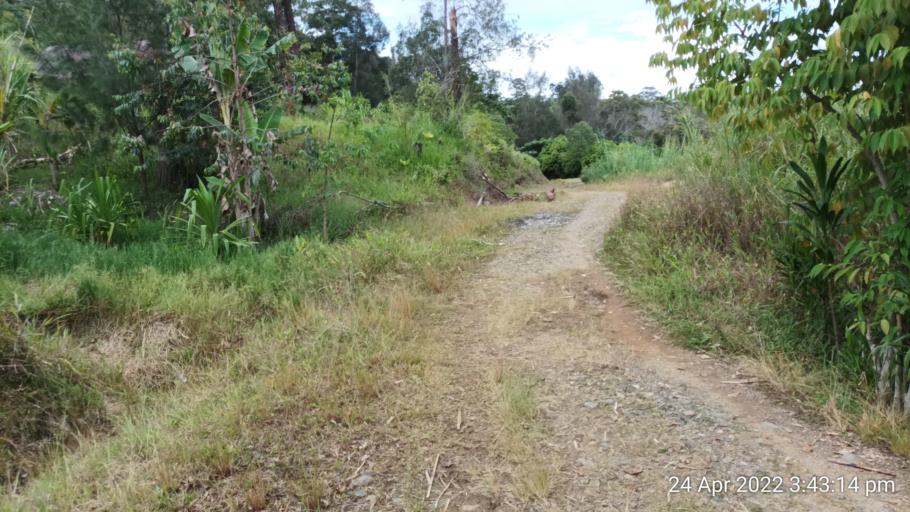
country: PG
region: Jiwaka
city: Minj
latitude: -5.8947
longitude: 144.8219
